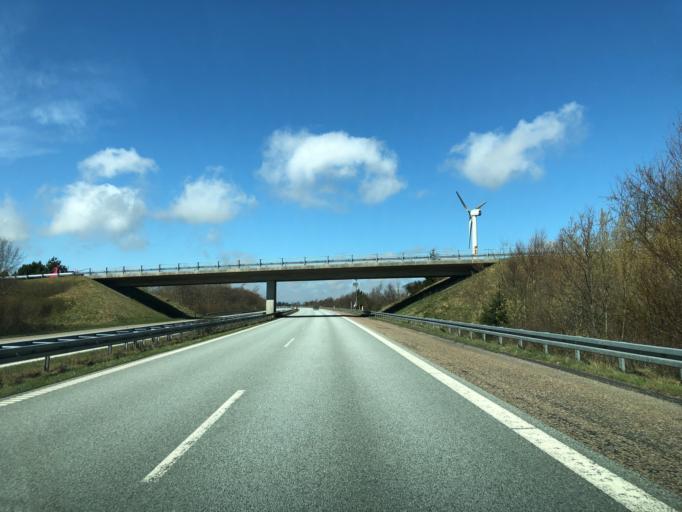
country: DK
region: North Denmark
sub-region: Hjorring Kommune
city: Hjorring
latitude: 57.4815
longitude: 10.0375
